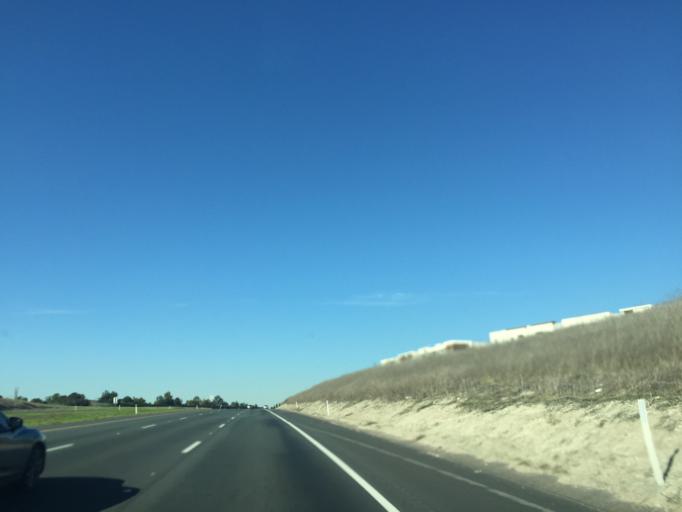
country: US
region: California
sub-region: San Diego County
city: Bonita
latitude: 32.6096
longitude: -116.9679
